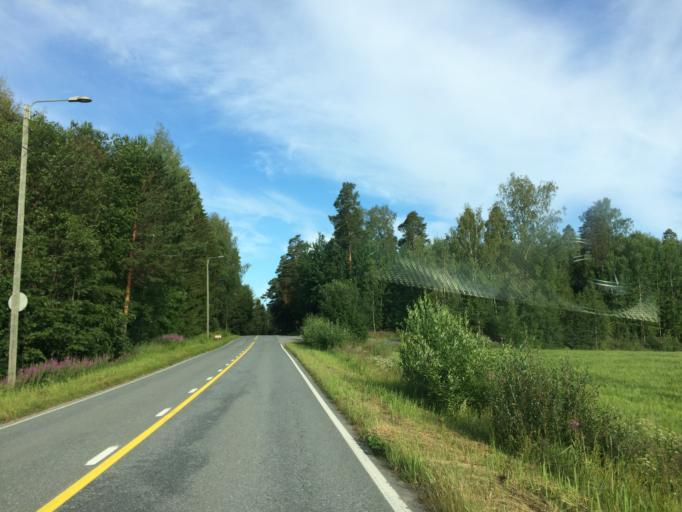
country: FI
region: Haeme
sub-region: Haemeenlinna
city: Janakkala
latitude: 60.9287
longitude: 24.5787
